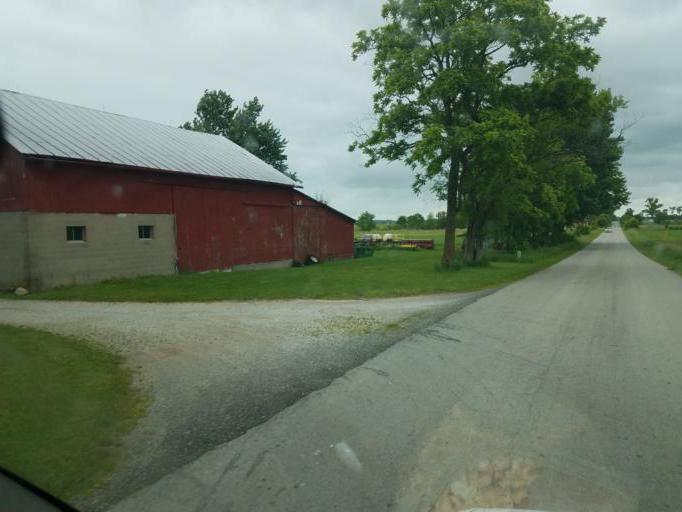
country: US
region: Ohio
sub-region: Morrow County
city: Cardington
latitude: 40.5483
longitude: -82.9004
